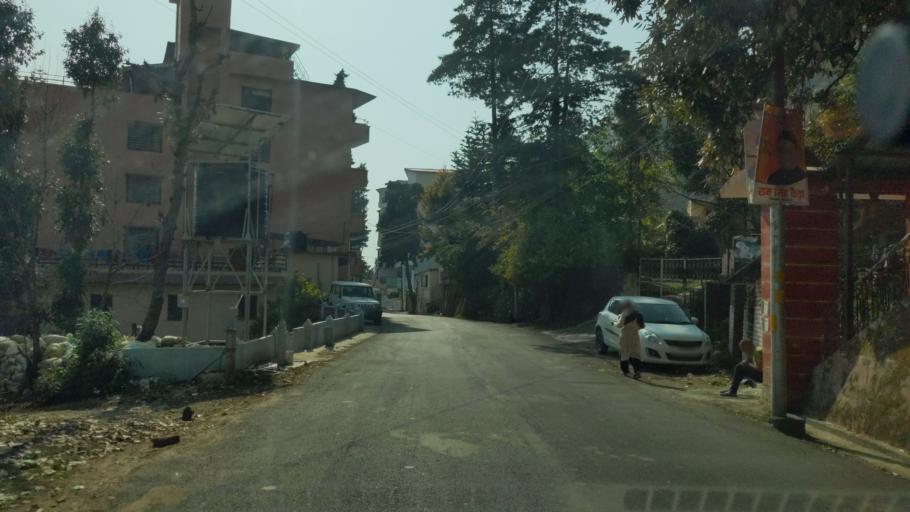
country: IN
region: Uttarakhand
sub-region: Naini Tal
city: Bhowali
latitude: 29.3891
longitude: 79.5309
